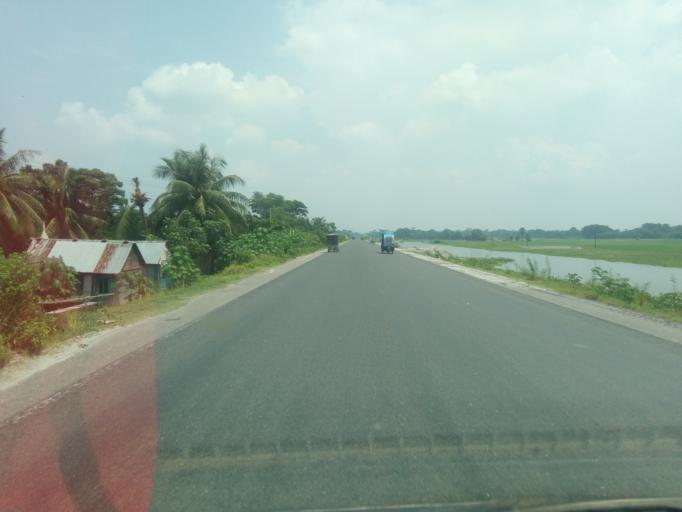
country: BD
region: Dhaka
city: Char Bhadrasan
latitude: 23.3791
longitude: 90.0101
